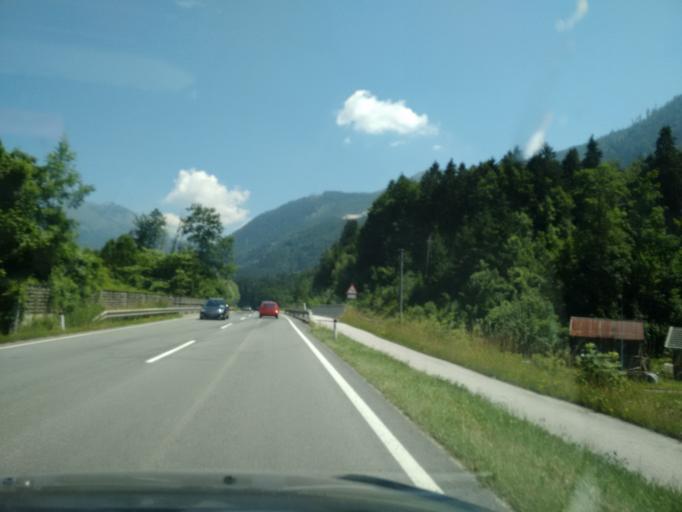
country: AT
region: Upper Austria
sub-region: Politischer Bezirk Gmunden
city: Ebensee
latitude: 47.7873
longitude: 13.7516
